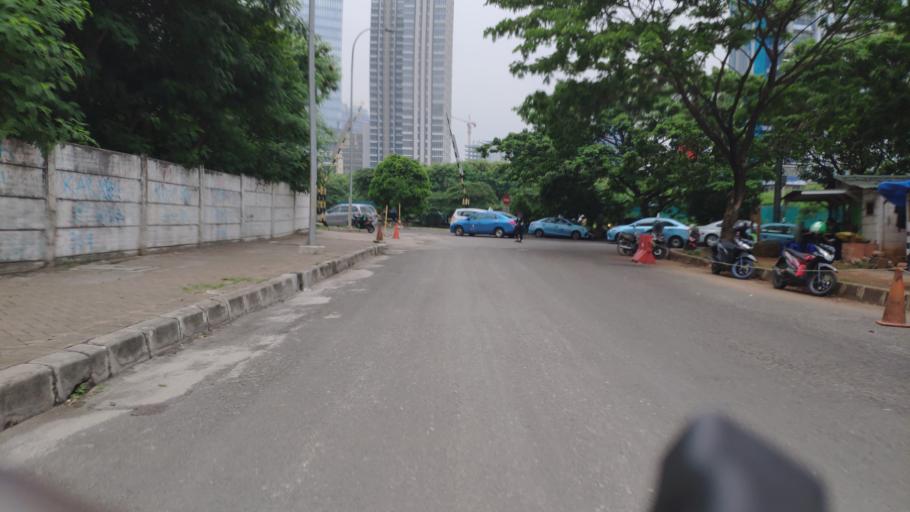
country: ID
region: Jakarta Raya
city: Jakarta
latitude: -6.2140
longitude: 106.8366
